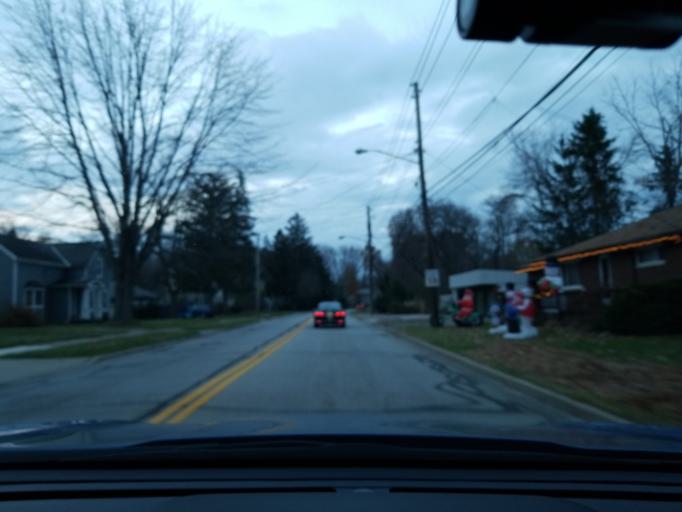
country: US
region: Ohio
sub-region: Cuyahoga County
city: Berea
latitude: 41.3611
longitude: -81.8612
